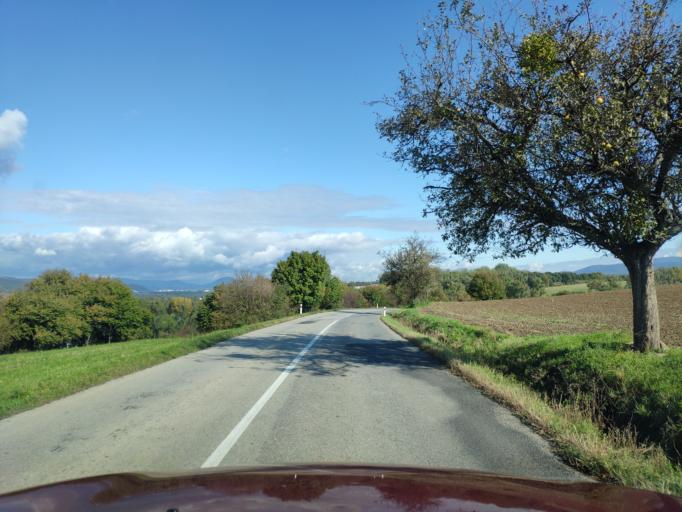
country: SK
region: Presovsky
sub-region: Okres Presov
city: Presov
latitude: 48.8975
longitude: 21.2597
